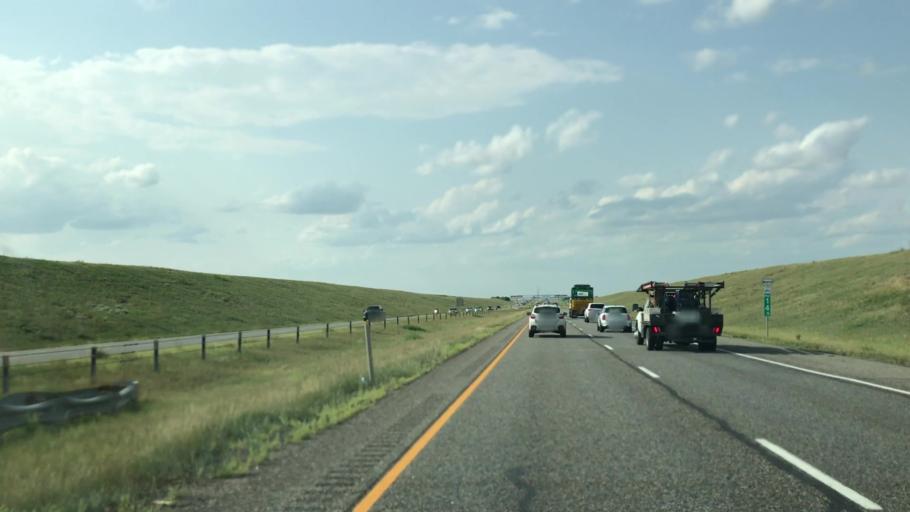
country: US
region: Colorado
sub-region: Arapahoe County
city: Dove Valley
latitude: 39.6548
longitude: -104.7205
